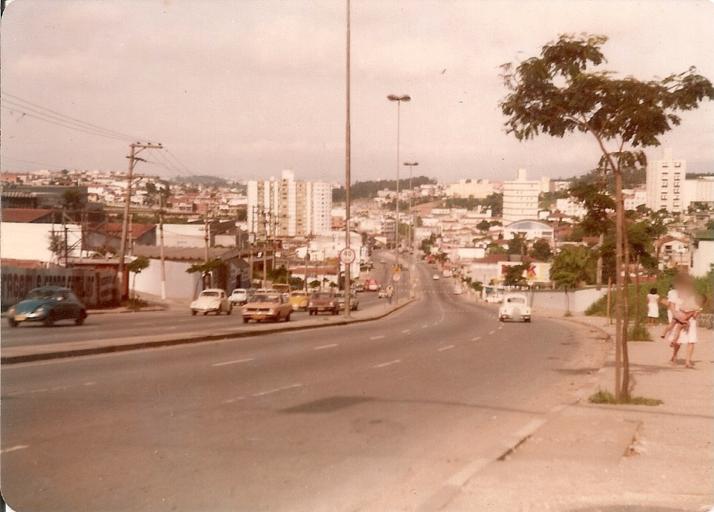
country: BR
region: Sao Paulo
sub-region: Diadema
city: Diadema
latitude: -23.6845
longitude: -46.6328
